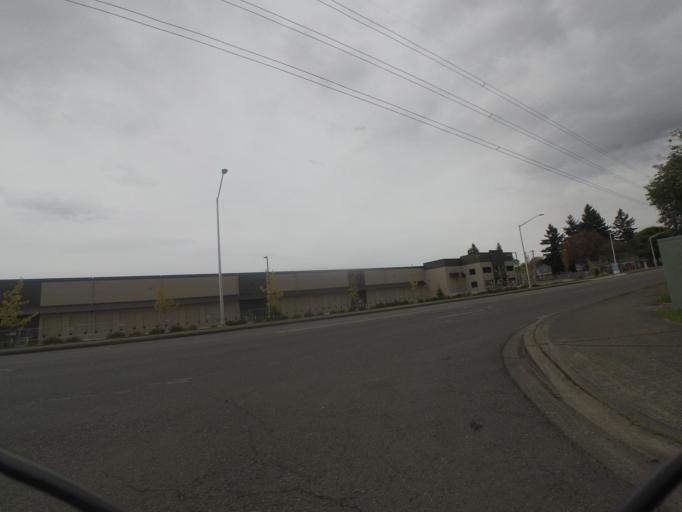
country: US
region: Washington
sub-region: Pierce County
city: Lakewood
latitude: 47.1810
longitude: -122.4809
